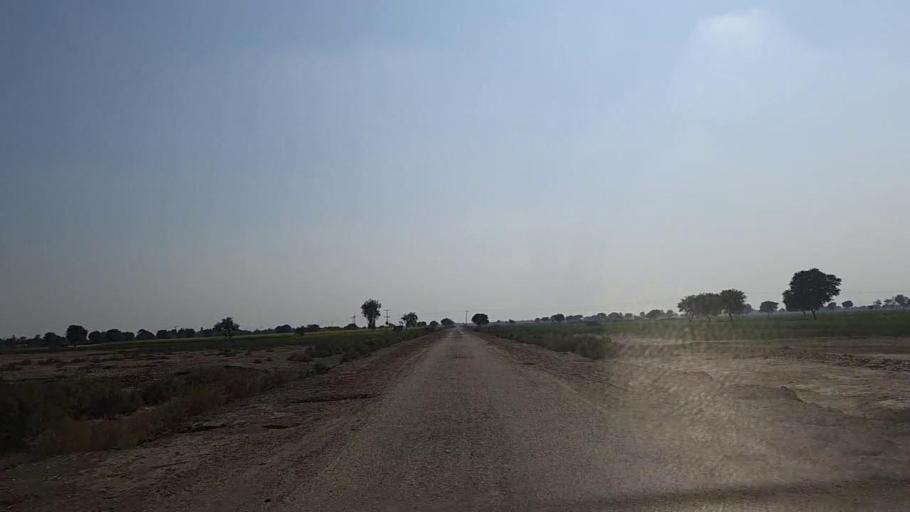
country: PK
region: Sindh
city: Jam Sahib
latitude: 26.2645
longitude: 68.5671
